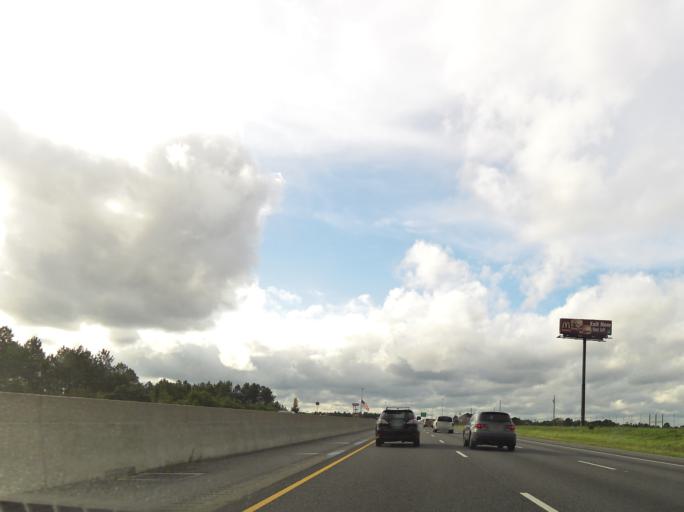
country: US
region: Georgia
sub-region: Turner County
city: Ashburn
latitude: 31.7041
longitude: -83.6340
